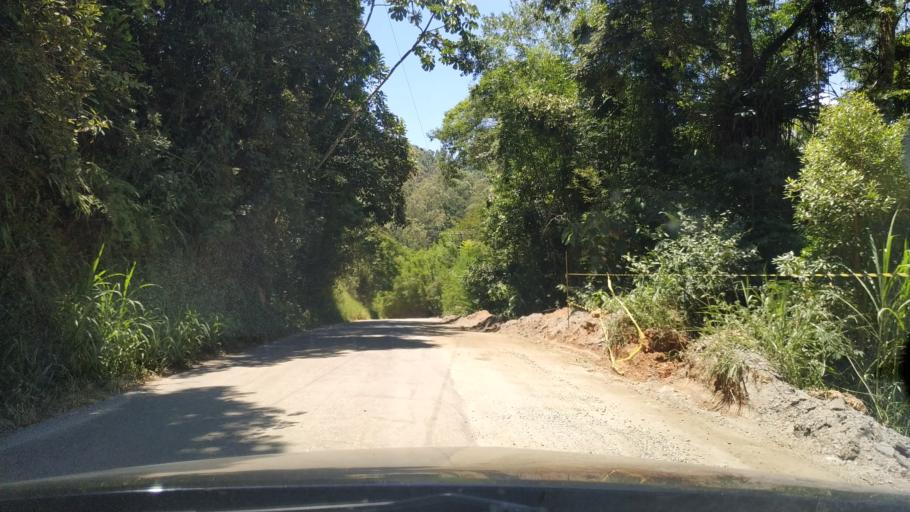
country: BR
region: Sao Paulo
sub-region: Campos Do Jordao
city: Campos do Jordao
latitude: -22.8060
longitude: -45.6901
